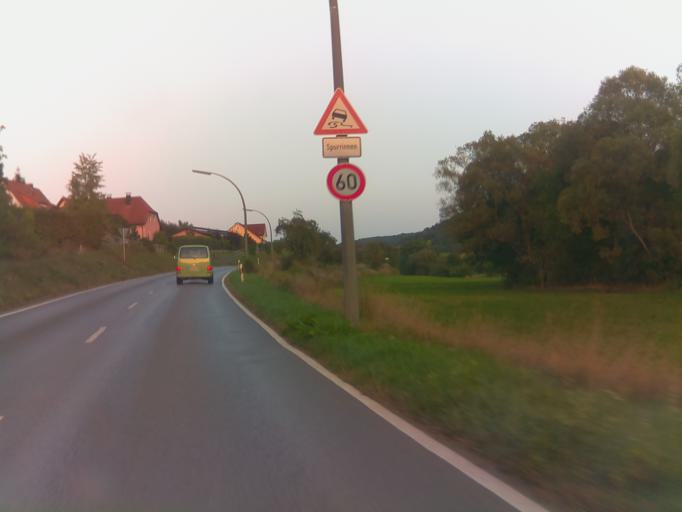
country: DE
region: Bavaria
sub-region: Regierungsbezirk Unterfranken
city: Euerdorf
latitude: 50.1430
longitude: 10.0281
